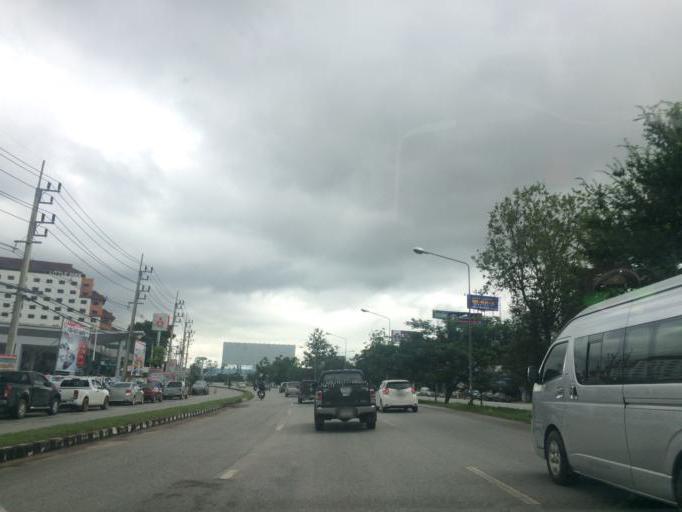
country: TH
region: Chiang Rai
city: Chiang Rai
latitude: 19.8778
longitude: 99.8320
